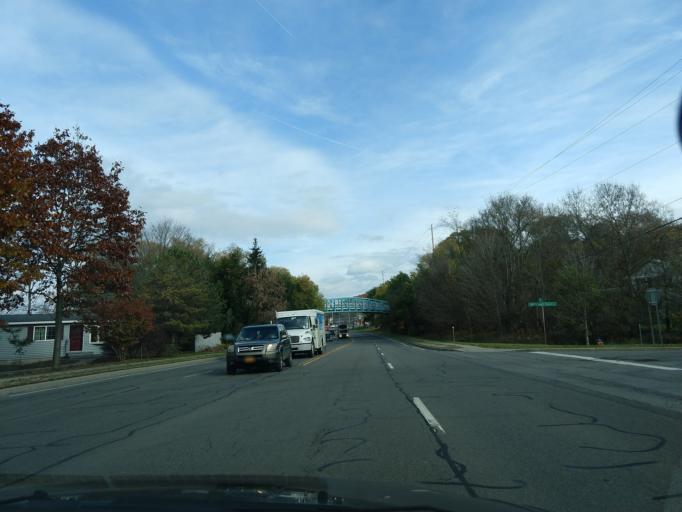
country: US
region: New York
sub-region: Tompkins County
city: South Hill
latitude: 42.4177
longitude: -76.5235
